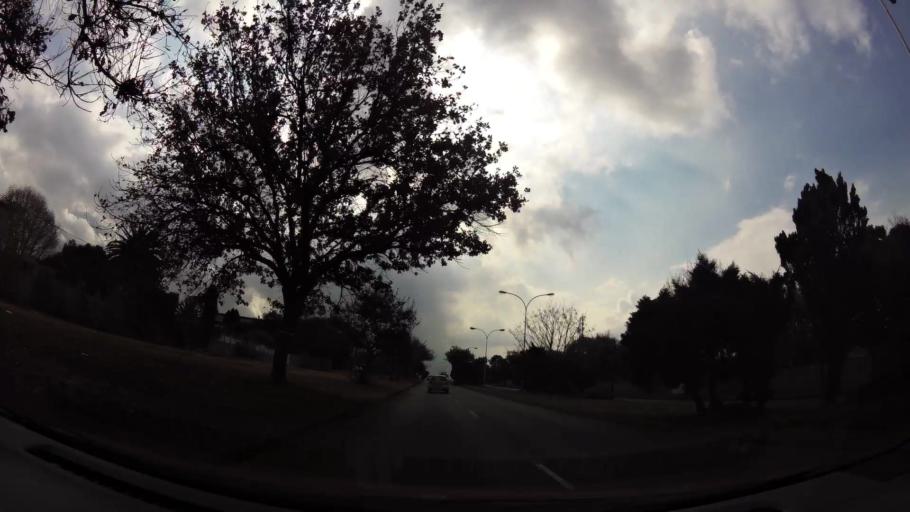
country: ZA
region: Gauteng
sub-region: Sedibeng District Municipality
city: Vanderbijlpark
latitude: -26.7283
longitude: 27.8373
